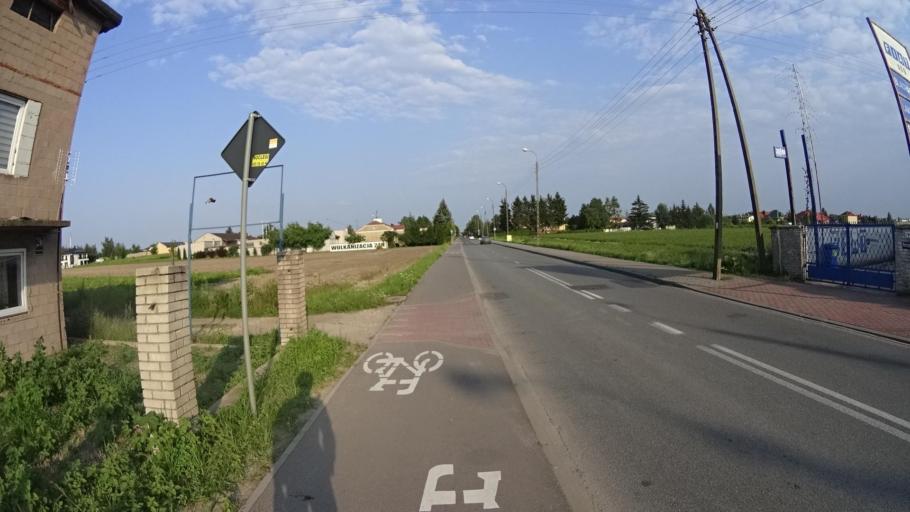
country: PL
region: Masovian Voivodeship
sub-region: Powiat pruszkowski
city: Rybie
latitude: 52.1494
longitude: 20.9385
